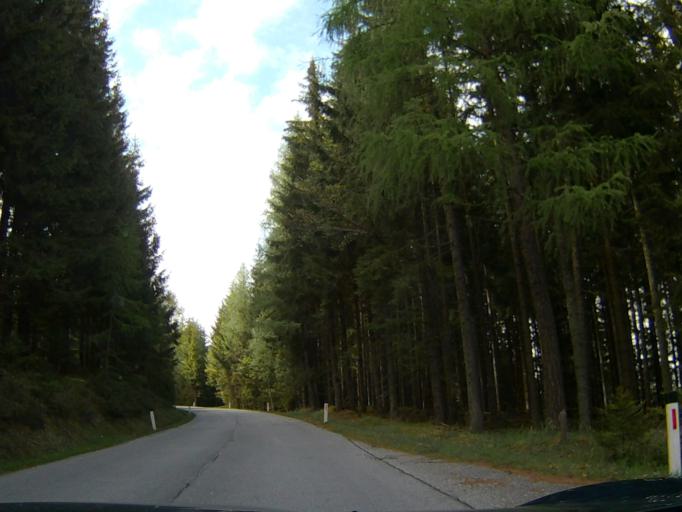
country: AT
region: Carinthia
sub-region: Politischer Bezirk Villach Land
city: Stockenboi
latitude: 46.7405
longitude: 13.5450
